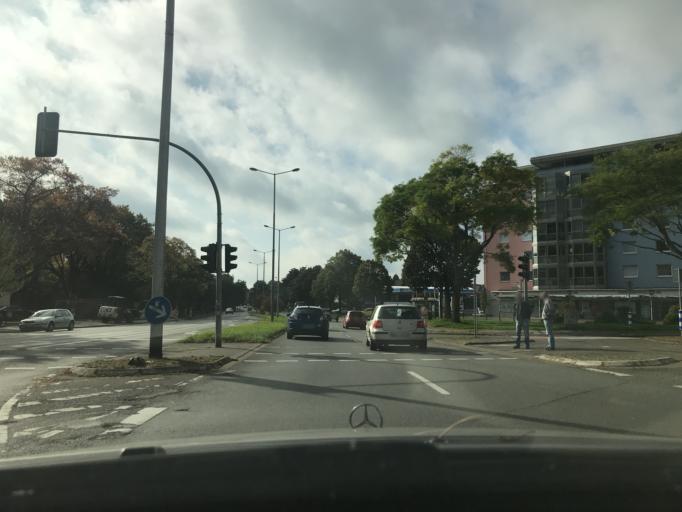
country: DE
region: North Rhine-Westphalia
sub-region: Regierungsbezirk Dusseldorf
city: Moers
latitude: 51.4530
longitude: 6.6215
